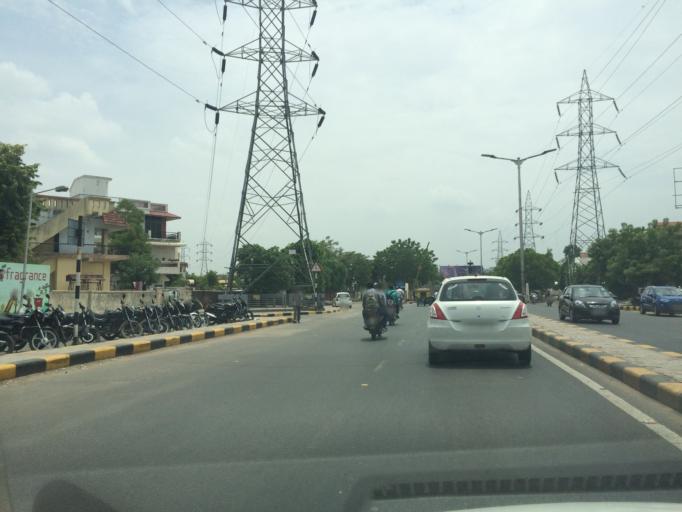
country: IN
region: Gujarat
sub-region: Ahmadabad
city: Ahmedabad
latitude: 23.0672
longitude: 72.5618
